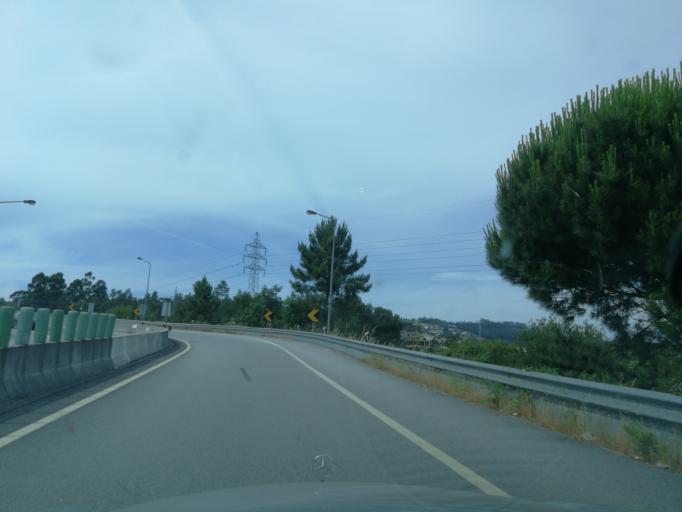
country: PT
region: Braga
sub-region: Vila Nova de Famalicao
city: Vila Nova de Famalicao
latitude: 41.4172
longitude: -8.5066
